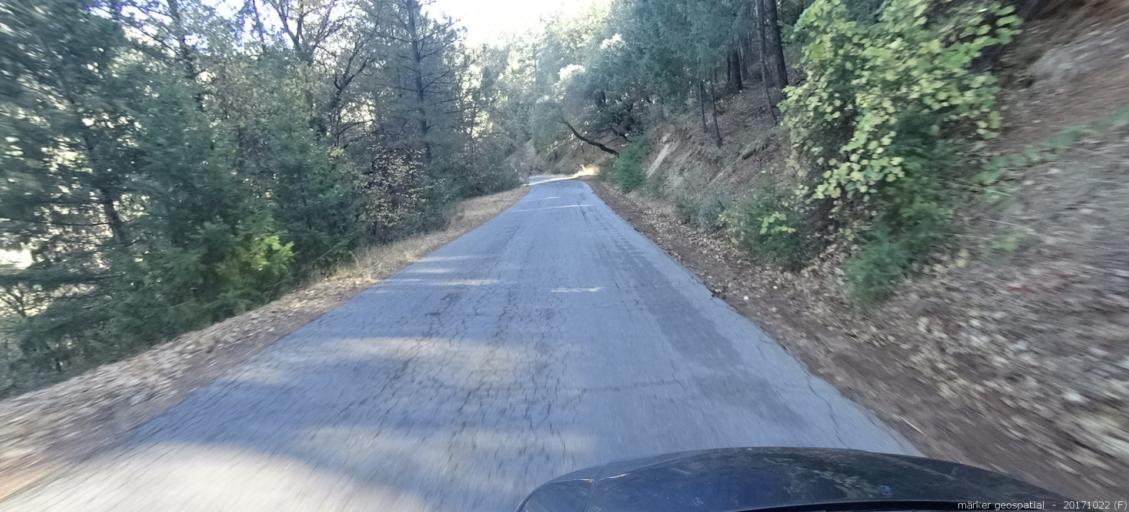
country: US
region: California
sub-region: Shasta County
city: Shasta Lake
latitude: 40.8705
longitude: -122.3626
